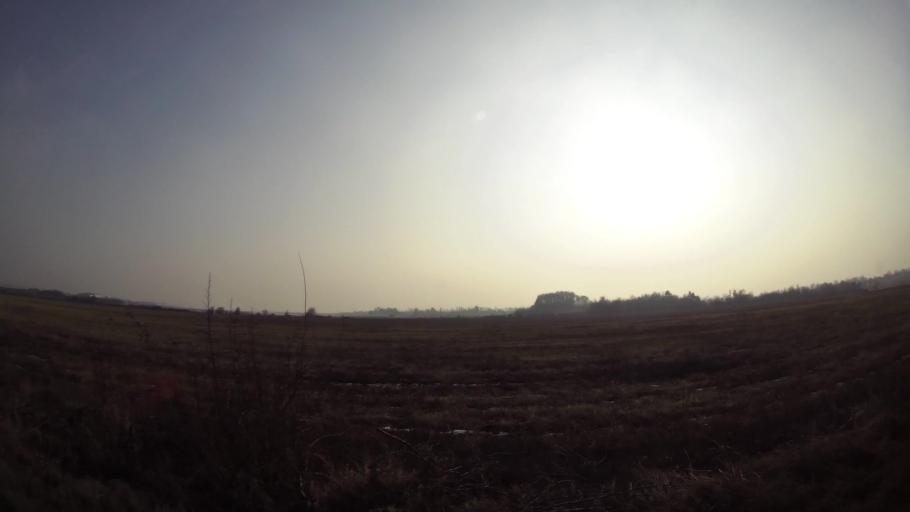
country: MK
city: Kadino
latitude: 41.9790
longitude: 21.6165
